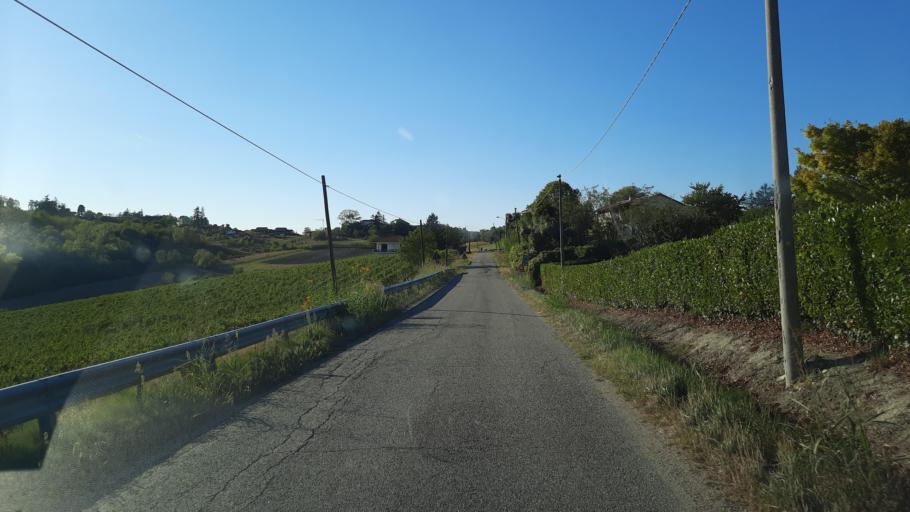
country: IT
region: Piedmont
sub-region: Provincia di Alessandria
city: Camagna Monferrato
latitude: 44.9984
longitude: 8.4300
